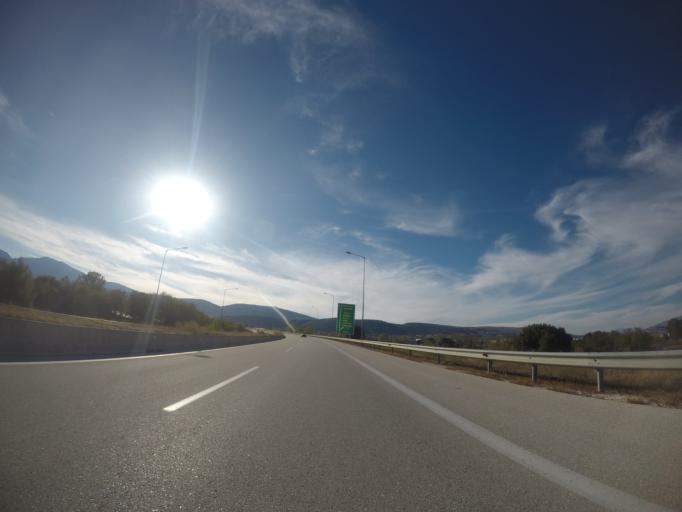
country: GR
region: Epirus
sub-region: Nomos Ioanninon
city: Katsikas
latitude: 39.6038
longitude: 20.8746
